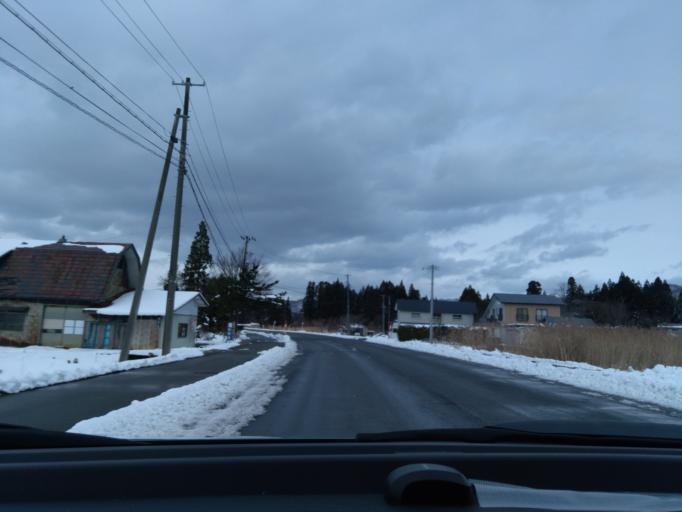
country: JP
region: Akita
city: Kakunodatemachi
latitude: 39.6196
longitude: 140.6314
